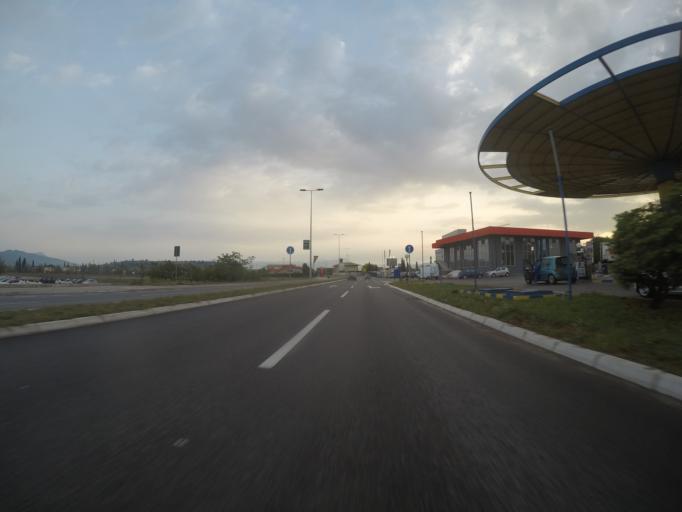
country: ME
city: Mojanovici
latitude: 42.3637
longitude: 19.2265
